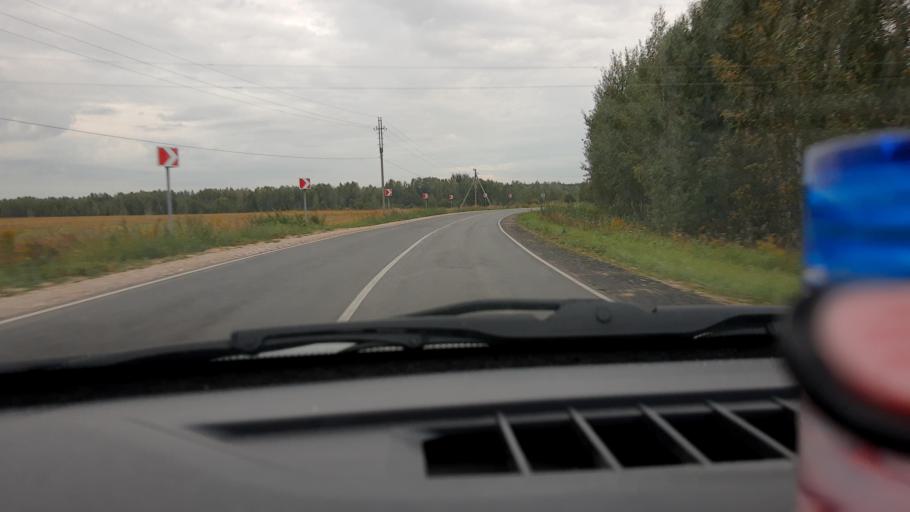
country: RU
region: Nizjnij Novgorod
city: Neklyudovo
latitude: 56.4561
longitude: 43.9060
